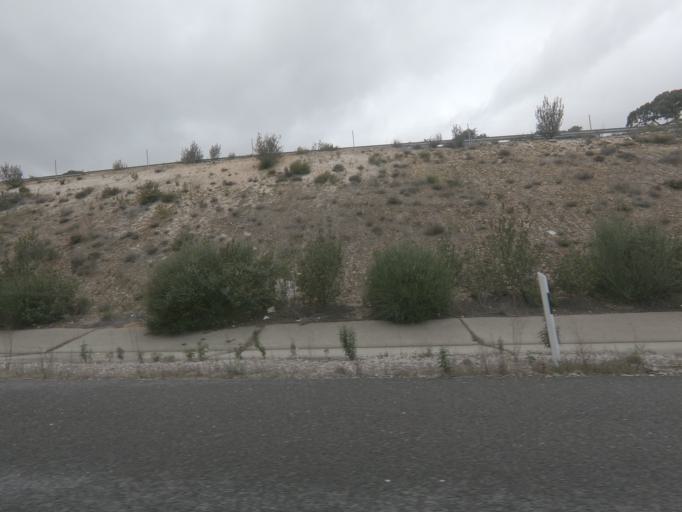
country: ES
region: Castille and Leon
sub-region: Provincia de Salamanca
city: Martinamor
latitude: 40.8167
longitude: -5.6368
